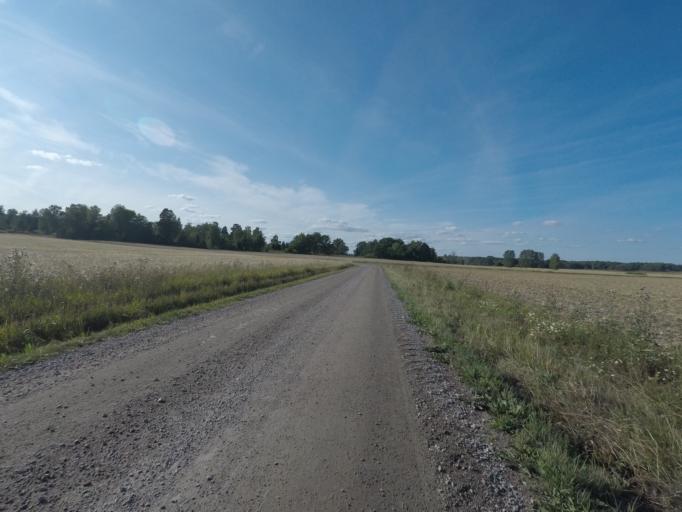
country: SE
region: Soedermanland
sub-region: Eskilstuna Kommun
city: Kvicksund
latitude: 59.4283
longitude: 16.3239
